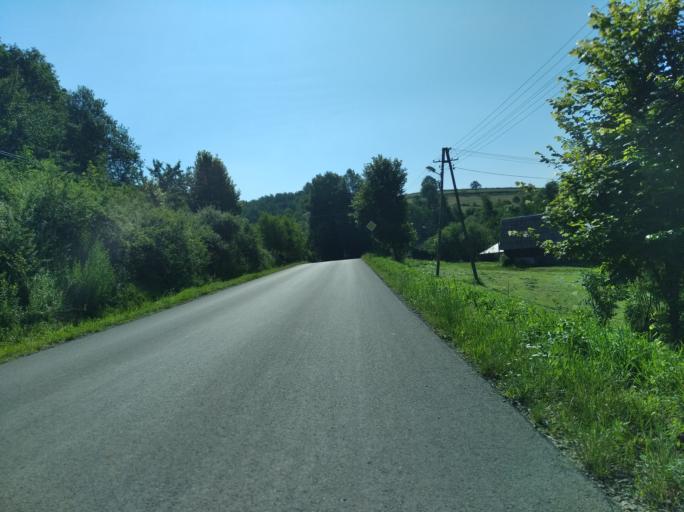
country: PL
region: Subcarpathian Voivodeship
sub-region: Powiat brzozowski
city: Nozdrzec
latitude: 49.8259
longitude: 22.1618
